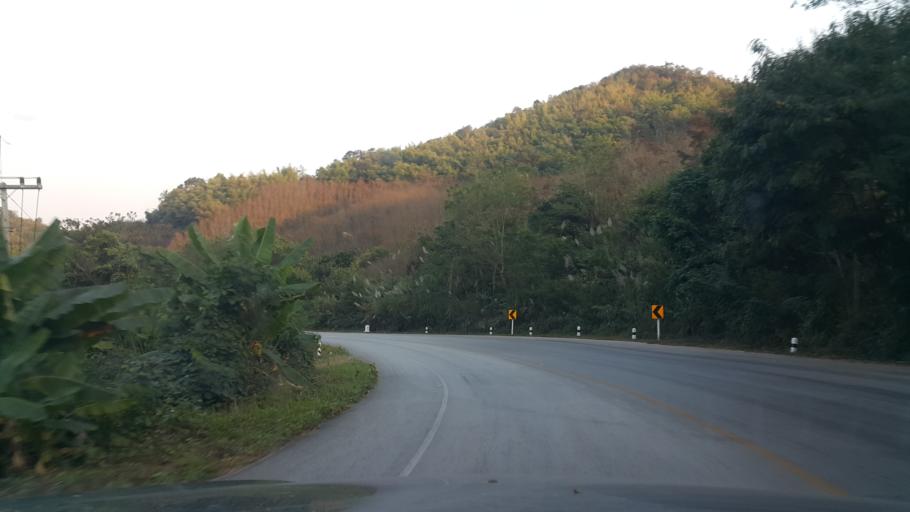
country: TH
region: Loei
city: Loei
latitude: 17.4785
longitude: 101.5524
